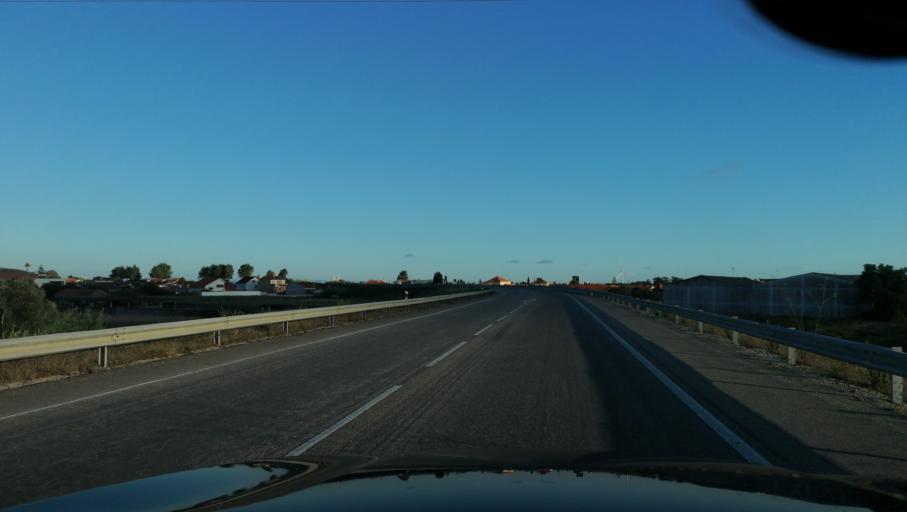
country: PT
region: Aveiro
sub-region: Aveiro
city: Oliveirinha
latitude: 40.5944
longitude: -8.6121
